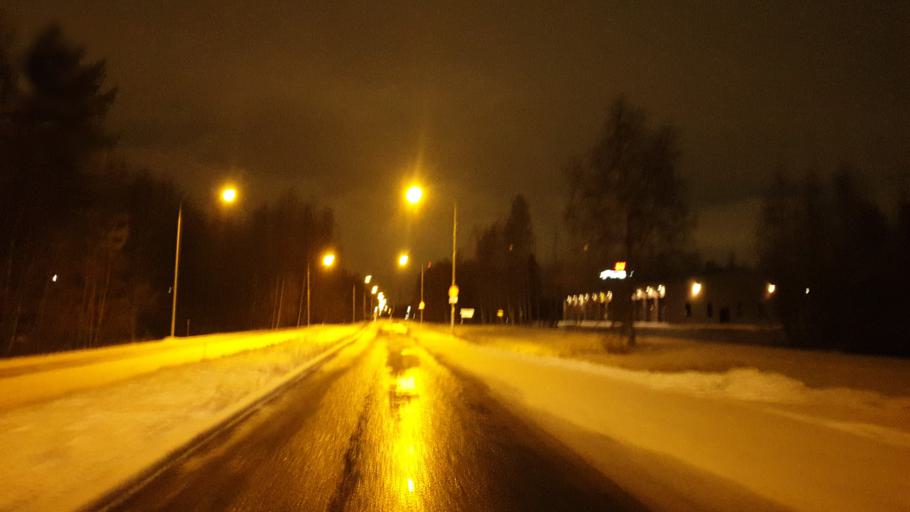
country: FI
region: Northern Ostrobothnia
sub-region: Oulu
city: Oulu
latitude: 64.9748
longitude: 25.4884
